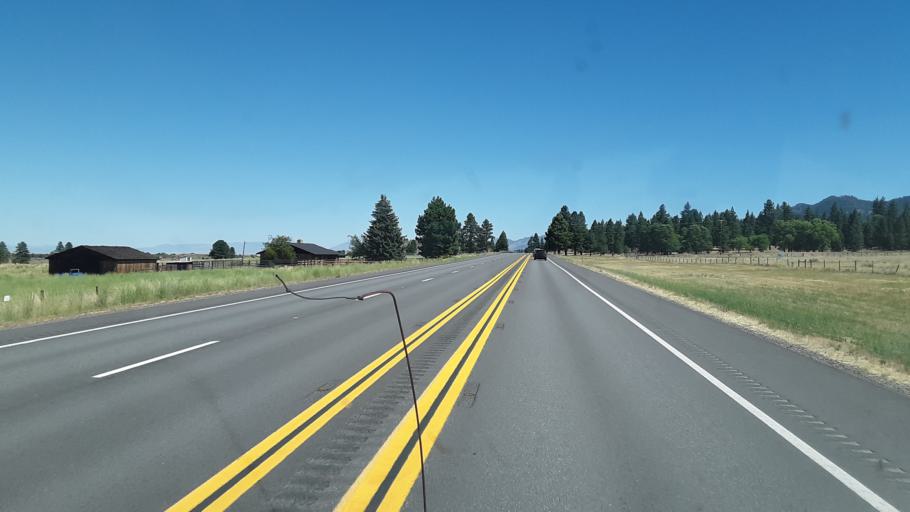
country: US
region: California
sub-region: Lassen County
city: Janesville
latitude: 40.3099
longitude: -120.5334
